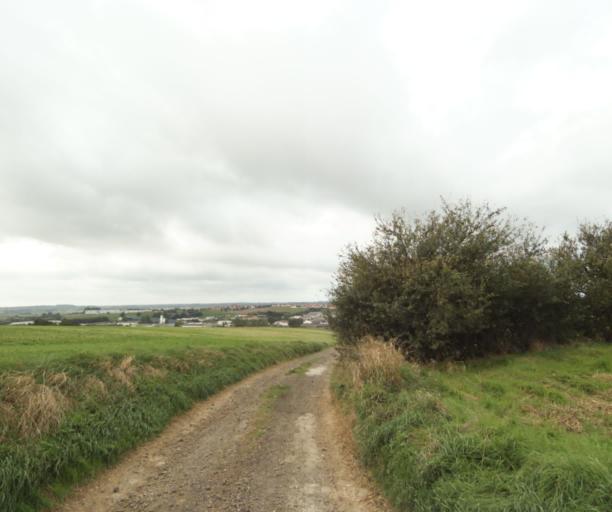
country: FR
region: Nord-Pas-de-Calais
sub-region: Departement du Pas-de-Calais
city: Etaples
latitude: 50.5259
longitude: 1.6663
